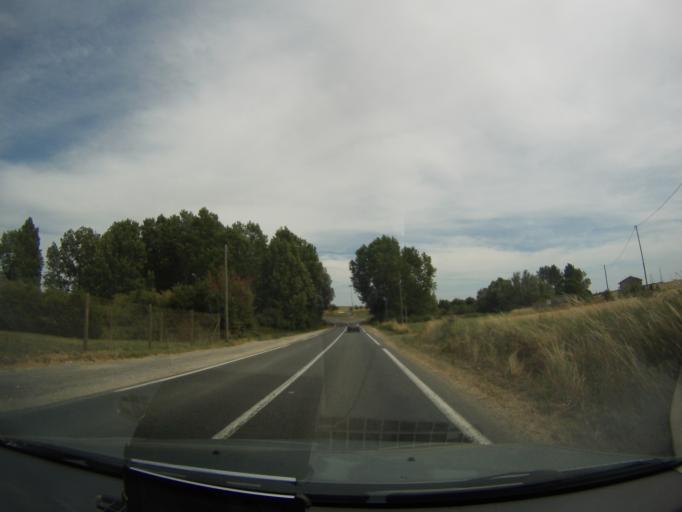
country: FR
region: Poitou-Charentes
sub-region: Departement de la Vienne
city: Mirebeau
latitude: 46.7808
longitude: 0.1335
